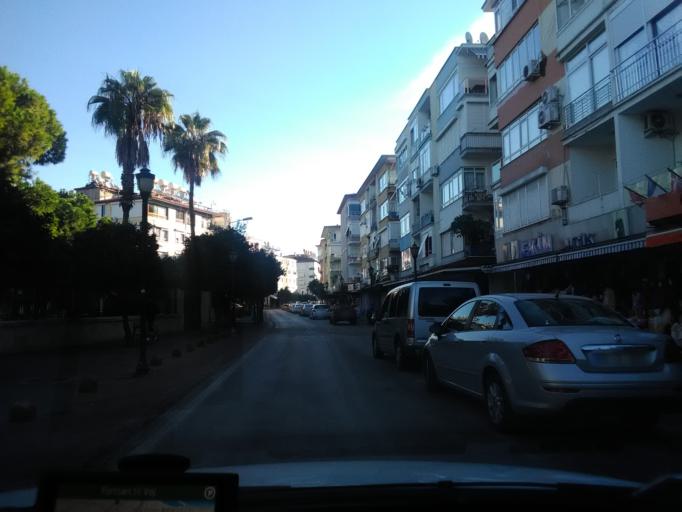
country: TR
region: Antalya
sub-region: Alanya
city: Alanya
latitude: 36.5435
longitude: 31.9885
